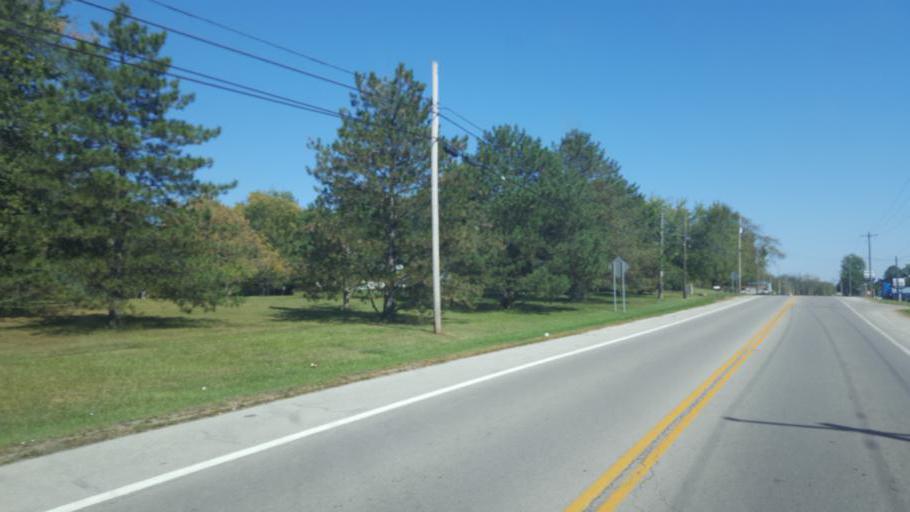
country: US
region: Ohio
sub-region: Crawford County
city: Galion
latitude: 40.7380
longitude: -82.7647
